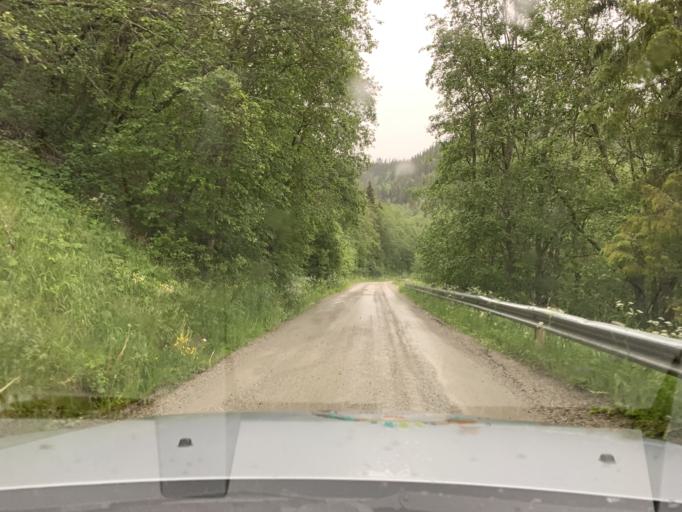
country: NO
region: Oppland
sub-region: Oyer
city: Tretten
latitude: 61.3918
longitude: 10.2724
